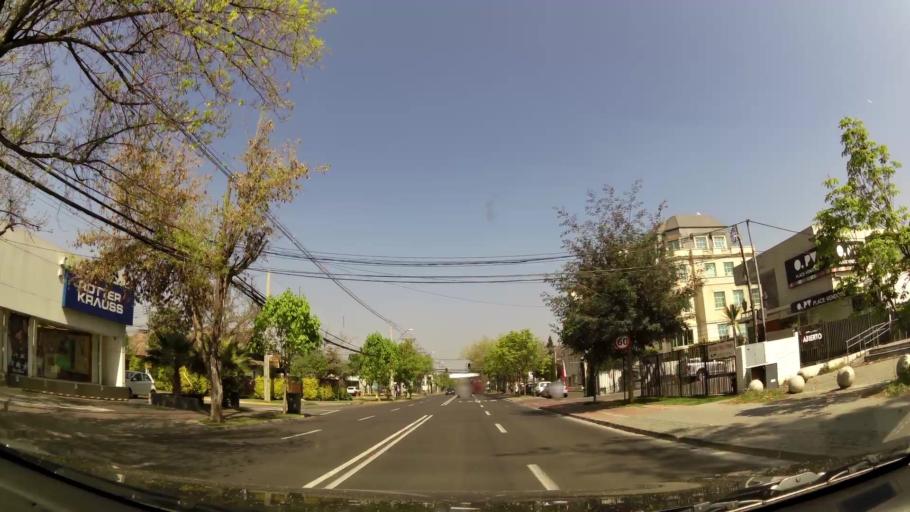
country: CL
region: Santiago Metropolitan
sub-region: Provincia de Santiago
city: Villa Presidente Frei, Nunoa, Santiago, Chile
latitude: -33.3882
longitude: -70.5774
